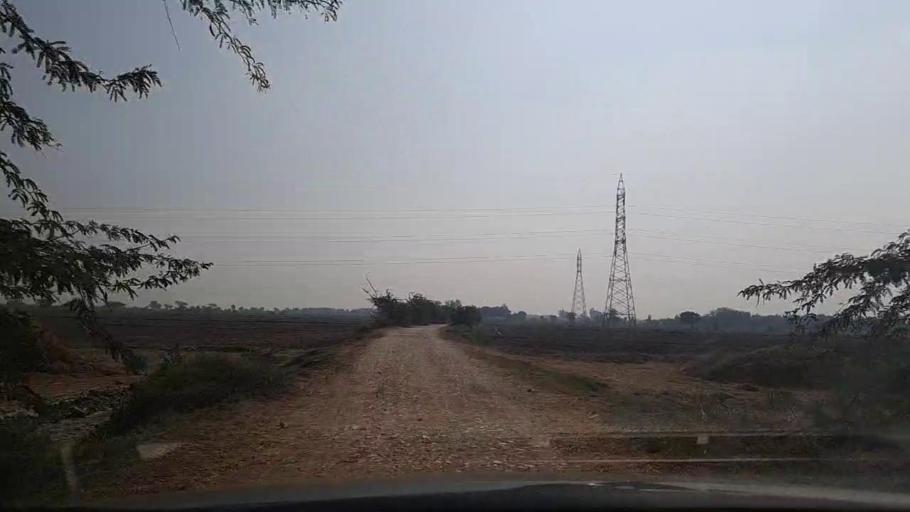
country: PK
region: Sindh
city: Mirpur Sakro
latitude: 24.5690
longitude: 67.7761
